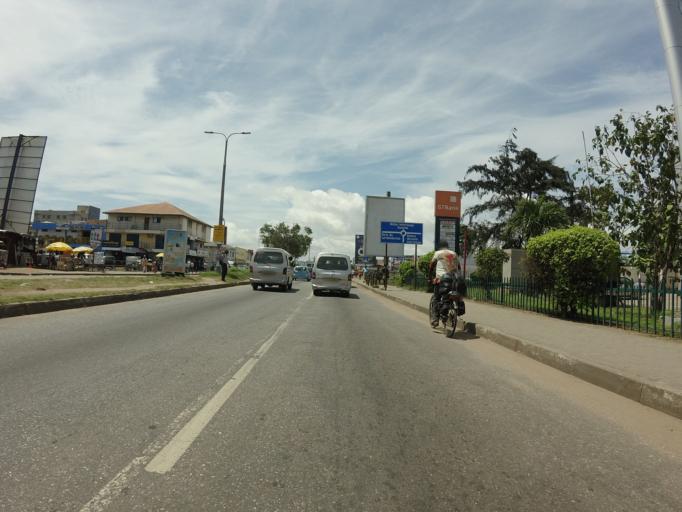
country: GH
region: Greater Accra
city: Accra
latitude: 5.5605
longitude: -0.2278
